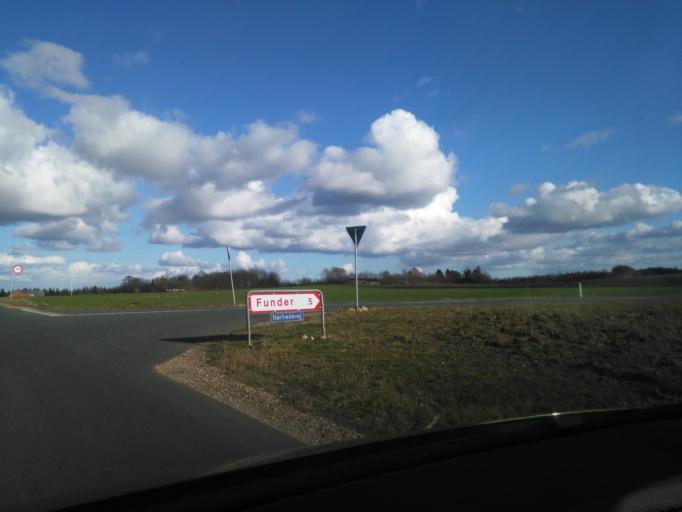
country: DK
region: Central Jutland
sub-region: Silkeborg Kommune
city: Silkeborg
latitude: 56.1917
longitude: 9.4681
